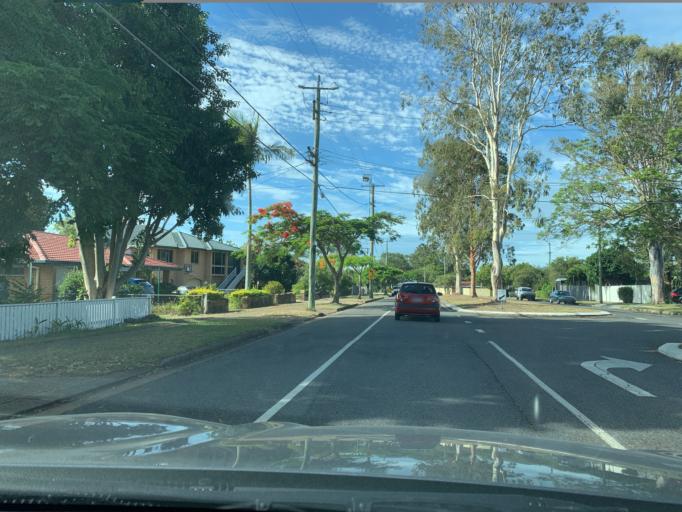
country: AU
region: Queensland
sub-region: Brisbane
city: Wynnum West
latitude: -27.4567
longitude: 153.1585
